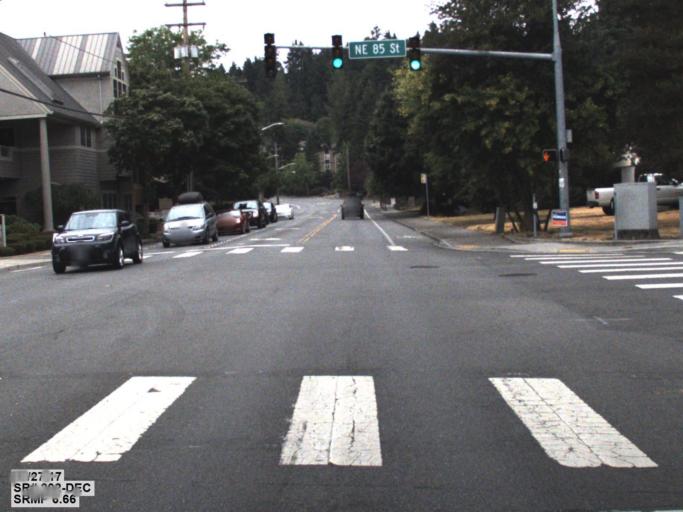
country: US
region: Washington
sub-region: King County
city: Redmond
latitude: 47.6784
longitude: -122.1216
